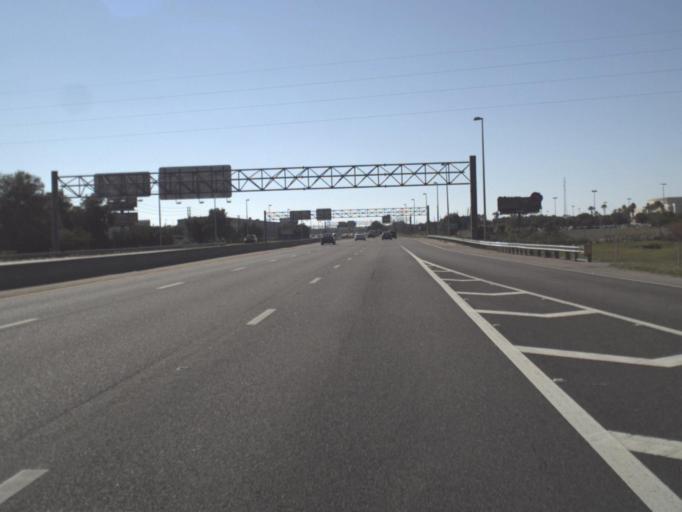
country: US
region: Florida
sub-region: Orange County
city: Sky Lake
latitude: 28.4437
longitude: -81.3868
